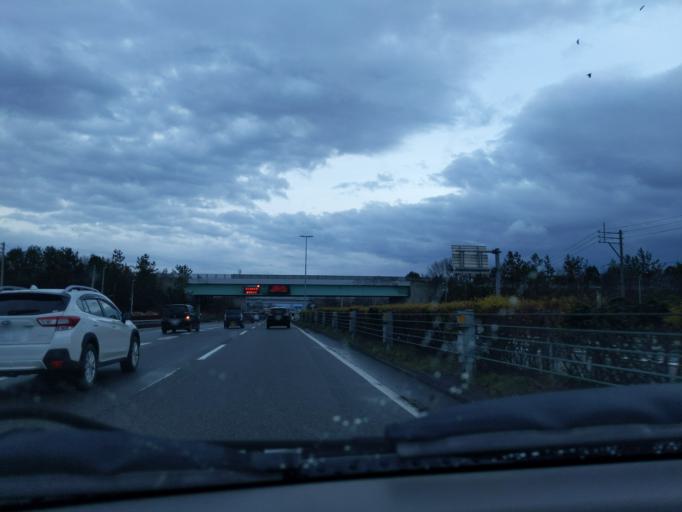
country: JP
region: Niigata
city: Kameda-honcho
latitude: 37.8819
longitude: 139.0809
